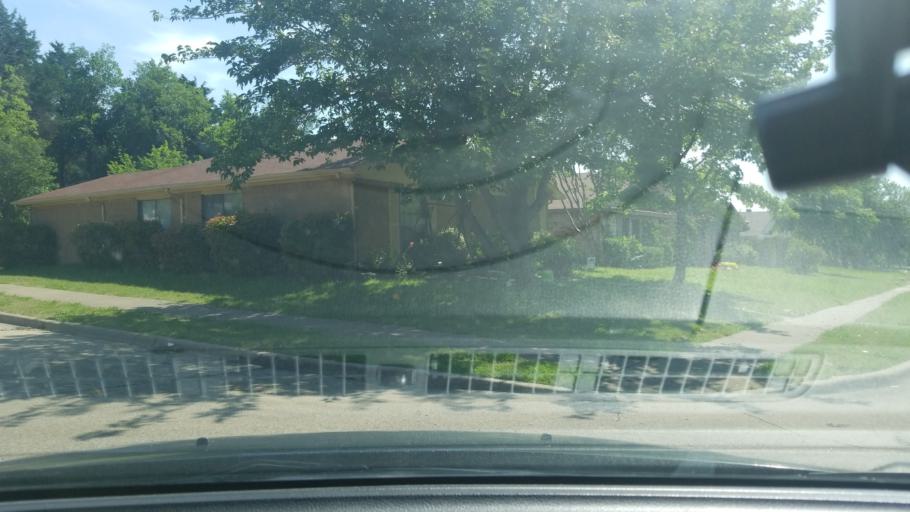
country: US
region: Texas
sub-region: Dallas County
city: Mesquite
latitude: 32.7775
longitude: -96.5940
